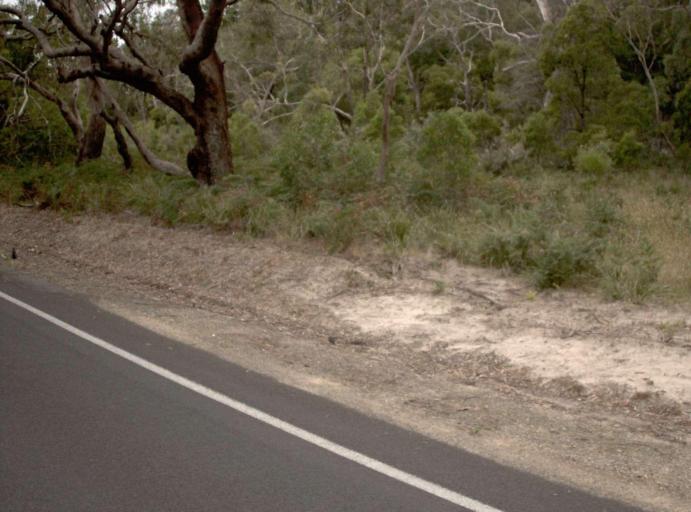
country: AU
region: Victoria
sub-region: Wellington
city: Sale
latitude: -38.2152
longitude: 147.0618
